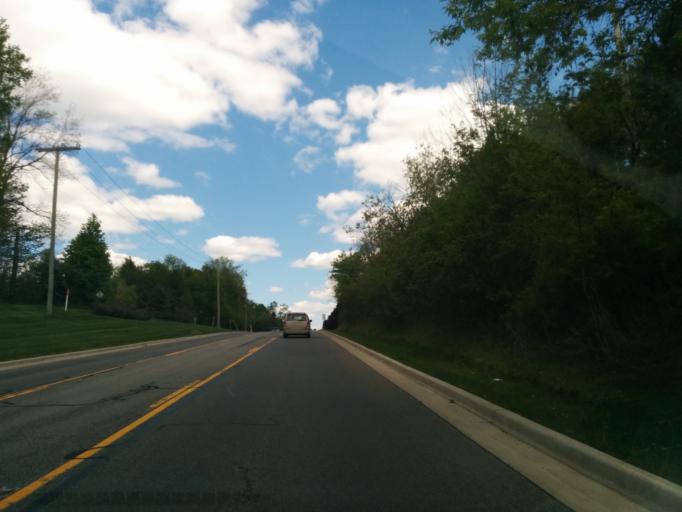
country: US
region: Michigan
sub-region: Oakland County
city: West Bloomfield Township
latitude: 42.5268
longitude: -83.4158
